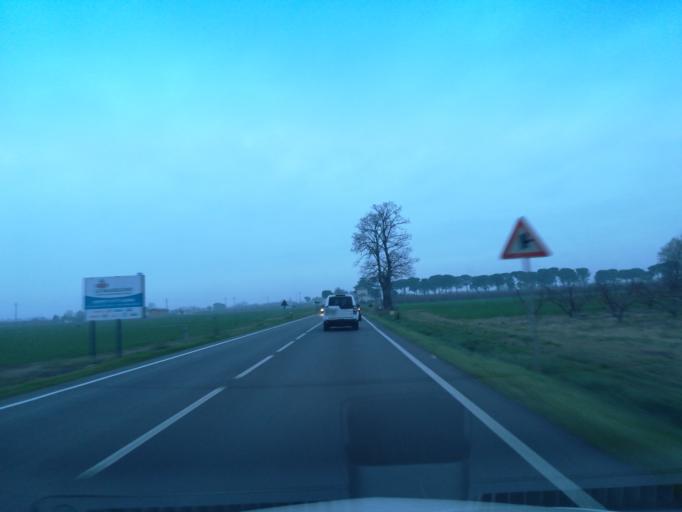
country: IT
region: Emilia-Romagna
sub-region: Provincia di Ravenna
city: Castel Bolognese
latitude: 44.3055
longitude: 11.8346
